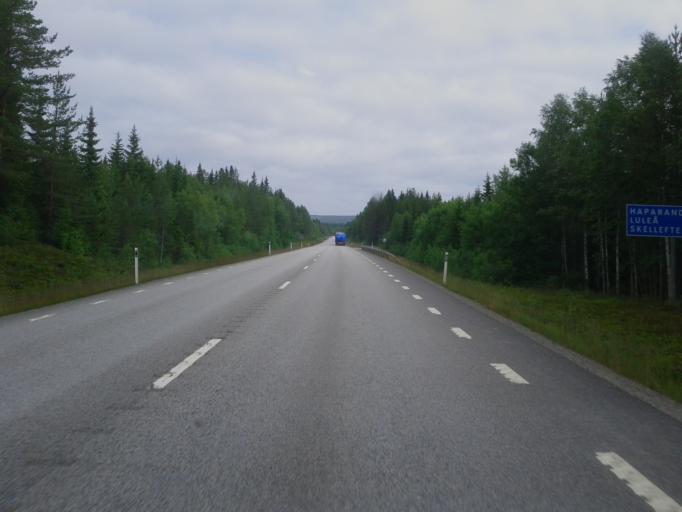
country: SE
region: Vaesterbotten
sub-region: Robertsfors Kommun
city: Robertsfors
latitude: 64.2828
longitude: 21.0677
